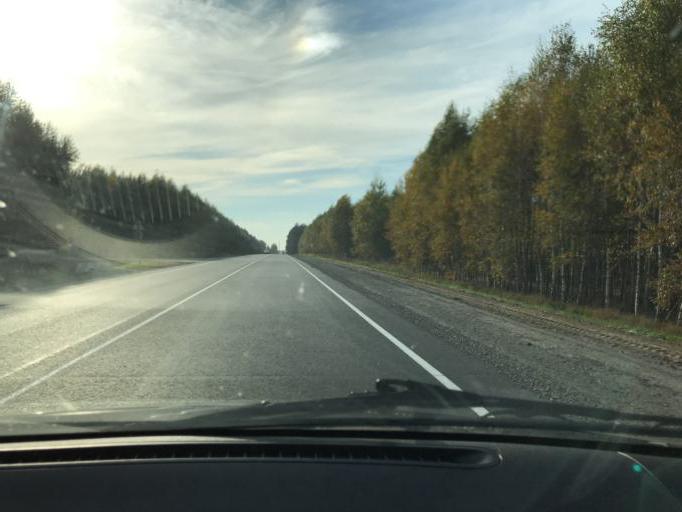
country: BY
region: Brest
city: Horad Pinsk
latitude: 52.1718
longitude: 26.0360
